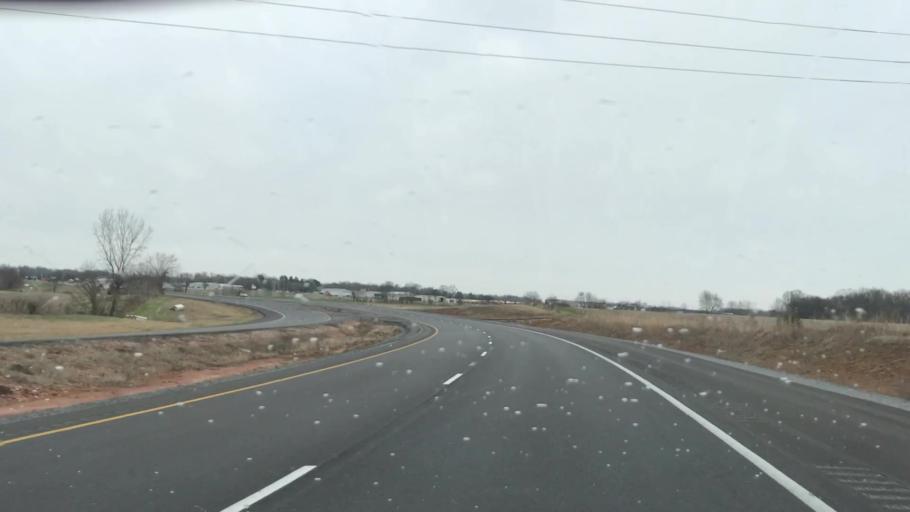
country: US
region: Kentucky
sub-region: Trigg County
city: Cadiz
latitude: 36.8612
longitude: -87.7998
